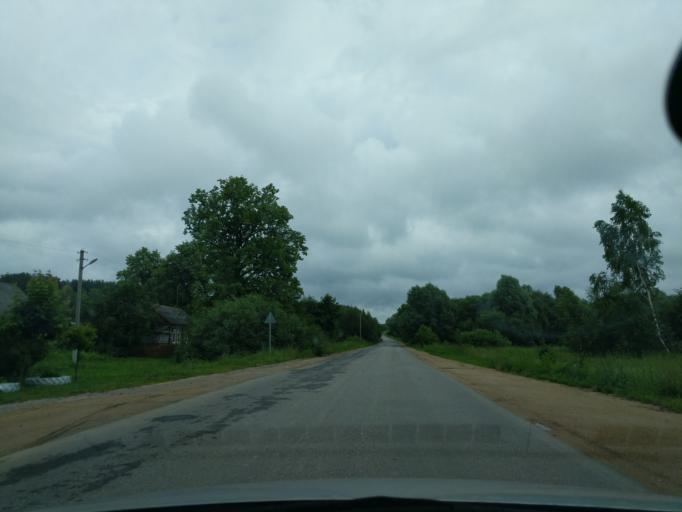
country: RU
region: Kaluga
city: Myatlevo
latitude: 54.8319
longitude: 35.6435
